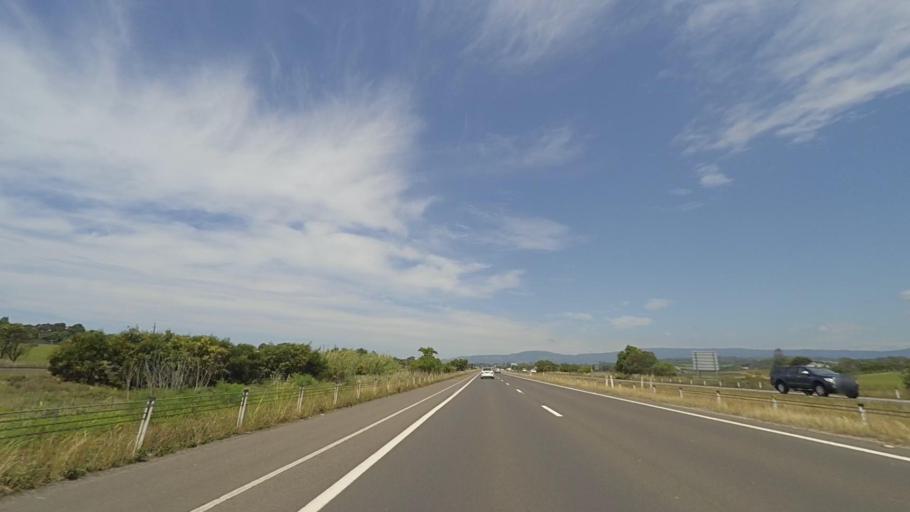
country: AU
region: New South Wales
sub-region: Shellharbour
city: Croom
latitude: -34.5996
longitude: 150.8413
